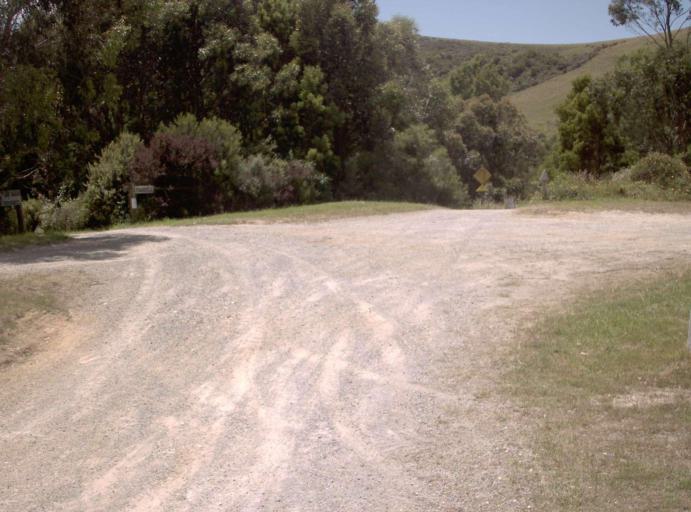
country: AU
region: Victoria
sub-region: Bass Coast
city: North Wonthaggi
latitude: -38.7159
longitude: 146.1124
